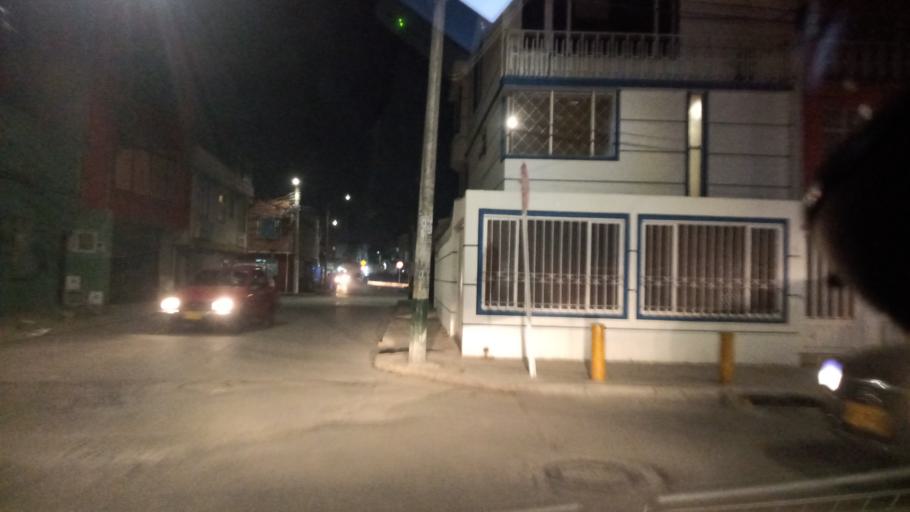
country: CO
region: Cundinamarca
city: Funza
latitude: 4.6775
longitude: -74.1509
